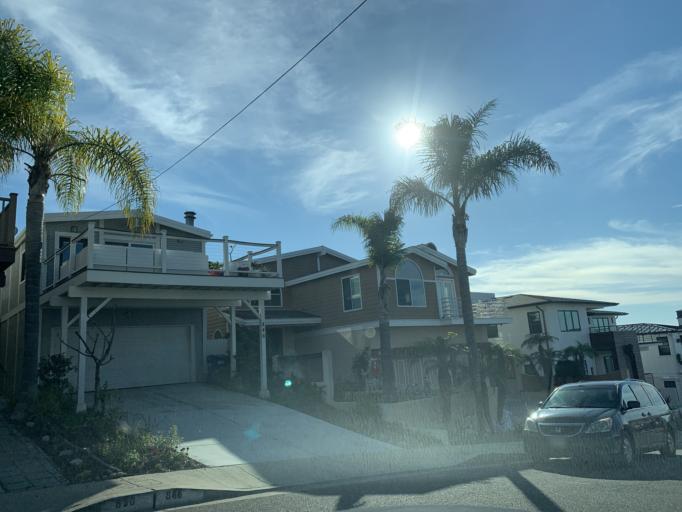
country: US
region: California
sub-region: Los Angeles County
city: Hermosa Beach
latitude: 33.8683
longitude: -118.3929
